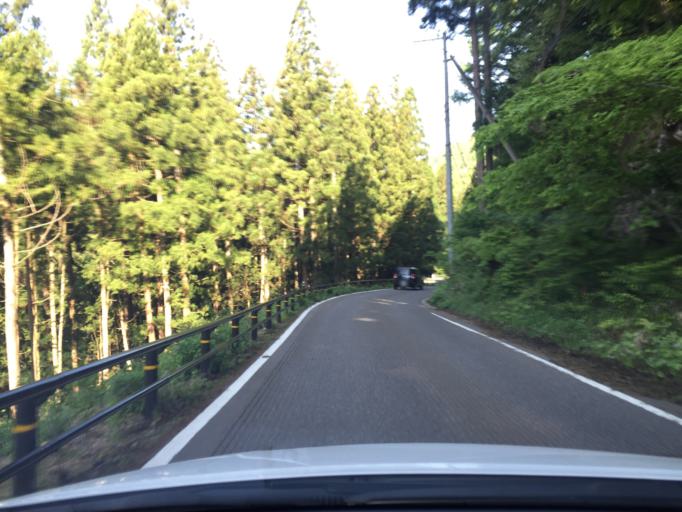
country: JP
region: Fukushima
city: Kitakata
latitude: 37.6660
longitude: 139.6134
